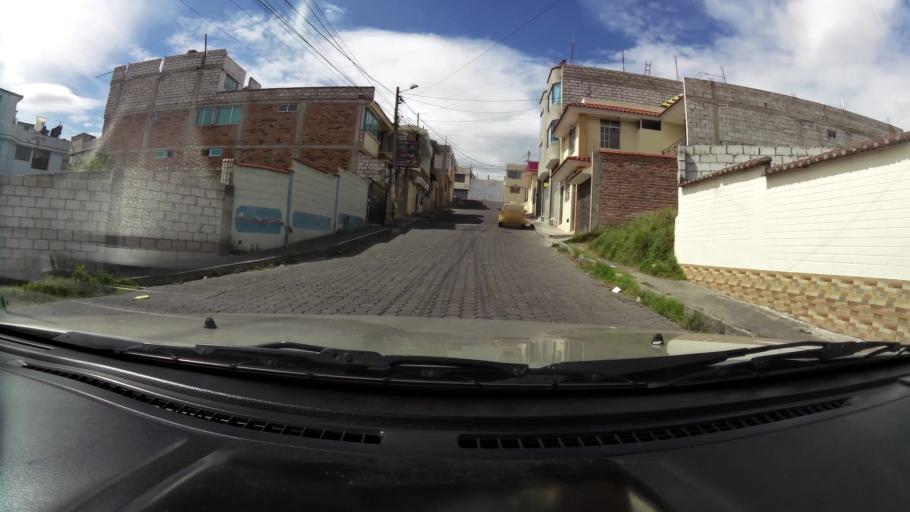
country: EC
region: Cotopaxi
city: Latacunga
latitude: -0.9299
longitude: -78.6042
